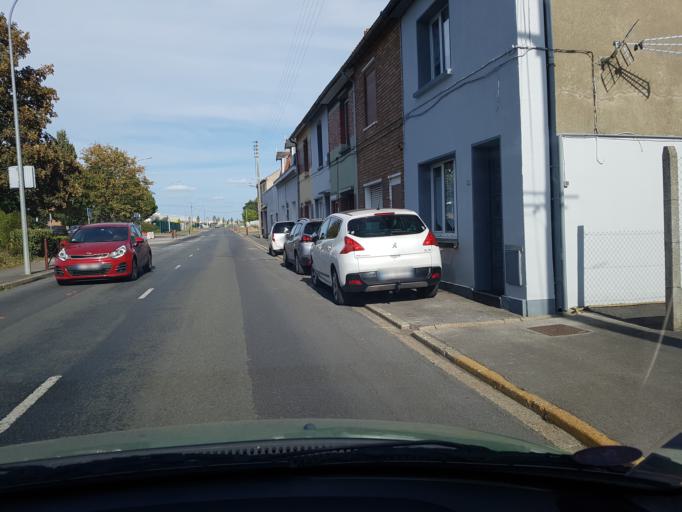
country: FR
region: Nord-Pas-de-Calais
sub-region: Departement du Pas-de-Calais
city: Fouquereuil
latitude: 50.5294
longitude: 2.5960
